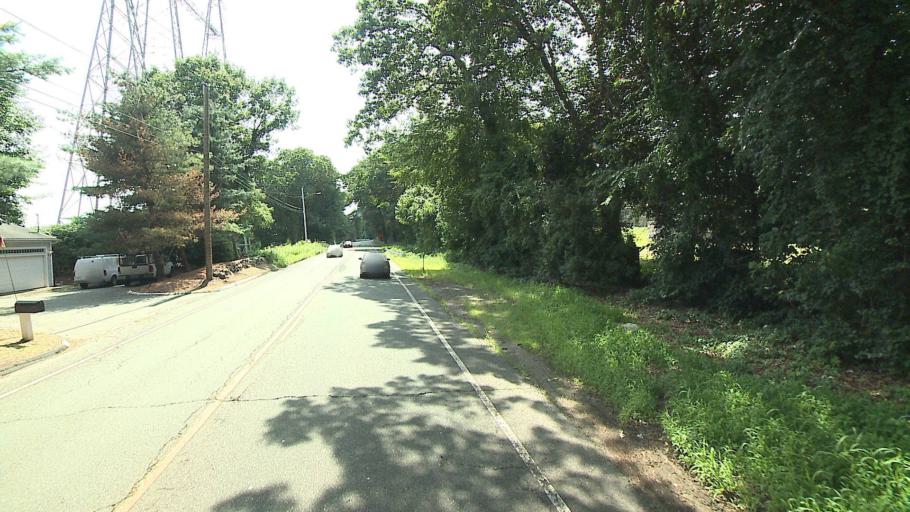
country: US
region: Connecticut
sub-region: New Haven County
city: City of Milford (balance)
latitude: 41.2307
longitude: -73.1111
